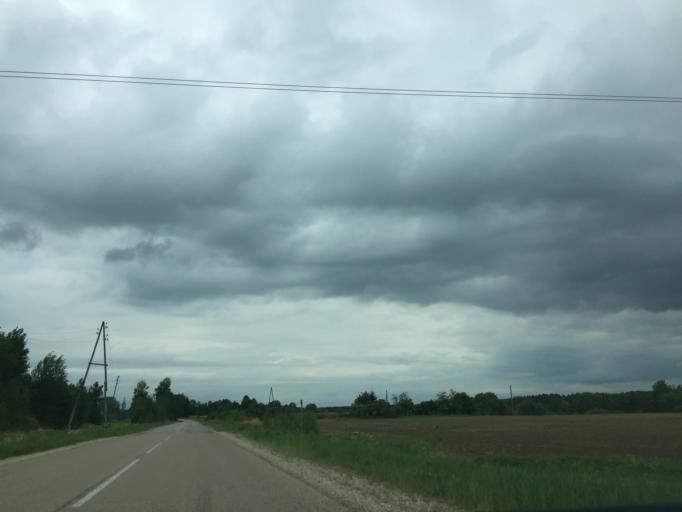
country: LV
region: Varkava
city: Vecvarkava
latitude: 56.0796
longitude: 26.6176
